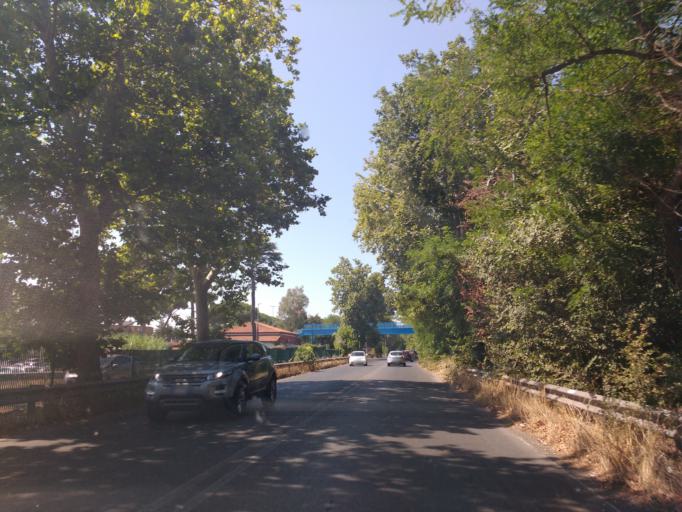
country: IT
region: Latium
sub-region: Citta metropolitana di Roma Capitale
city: Acilia-Castel Fusano-Ostia Antica
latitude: 41.7577
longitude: 12.3023
